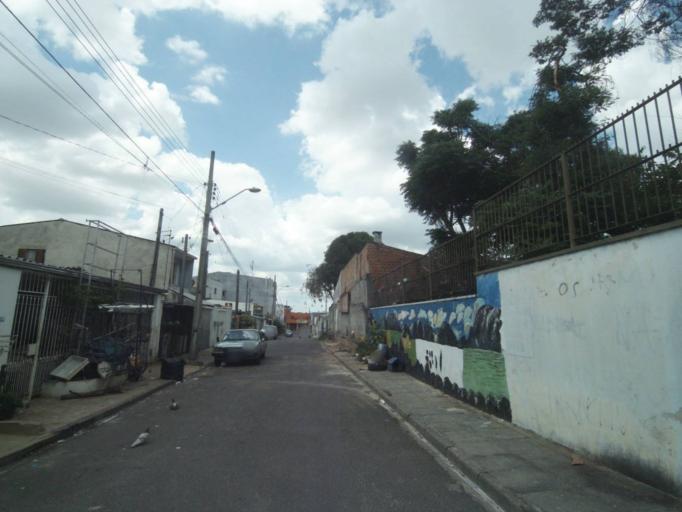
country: BR
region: Parana
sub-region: Sao Jose Dos Pinhais
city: Sao Jose dos Pinhais
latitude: -25.5342
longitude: -49.2756
